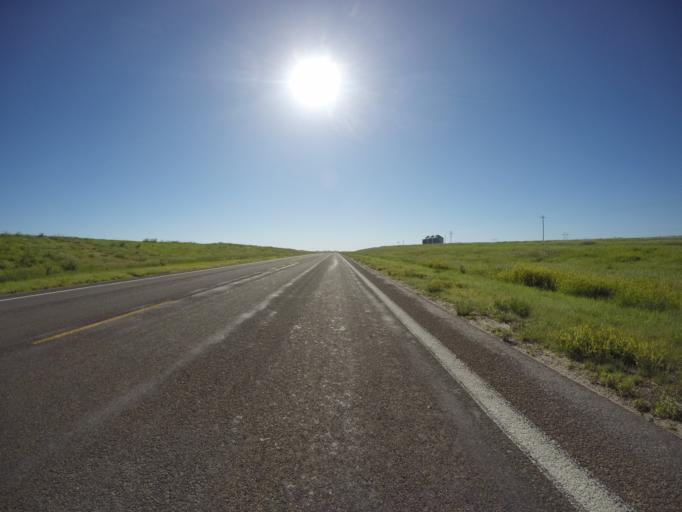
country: US
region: Kansas
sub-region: Norton County
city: Norton
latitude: 39.8281
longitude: -100.0341
